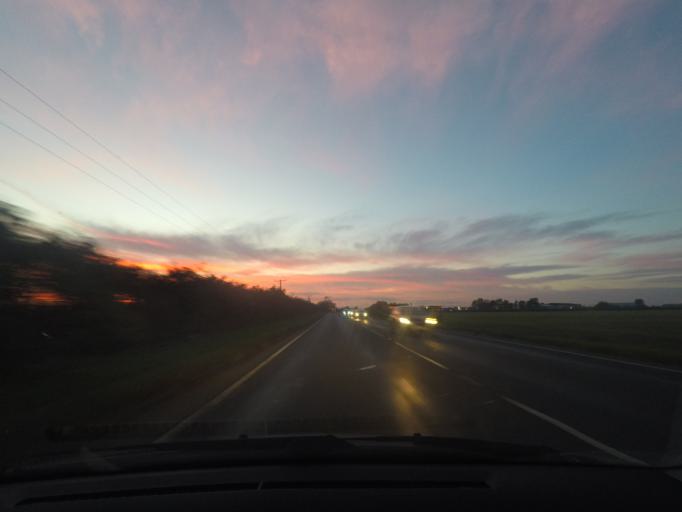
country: GB
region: England
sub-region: East Riding of Yorkshire
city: Pocklington
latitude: 53.9191
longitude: -0.7904
